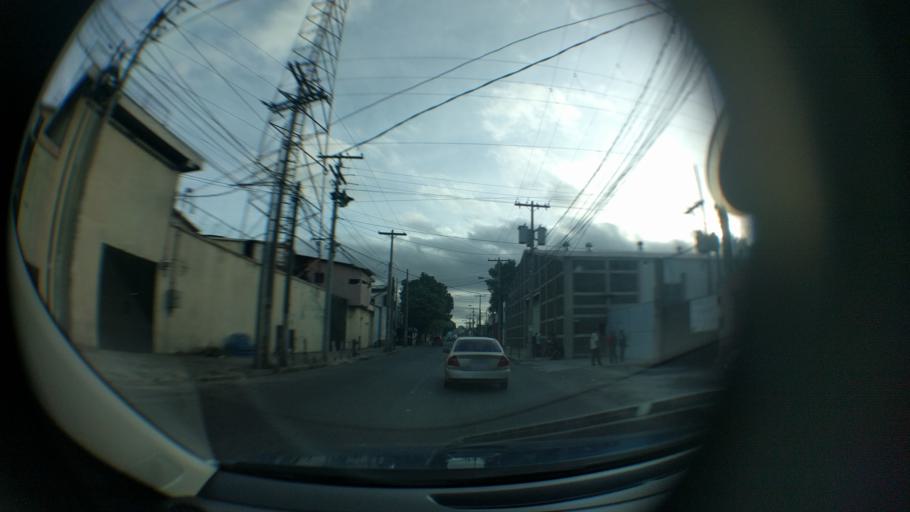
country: GT
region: Guatemala
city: Mixco
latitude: 14.5889
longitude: -90.5599
